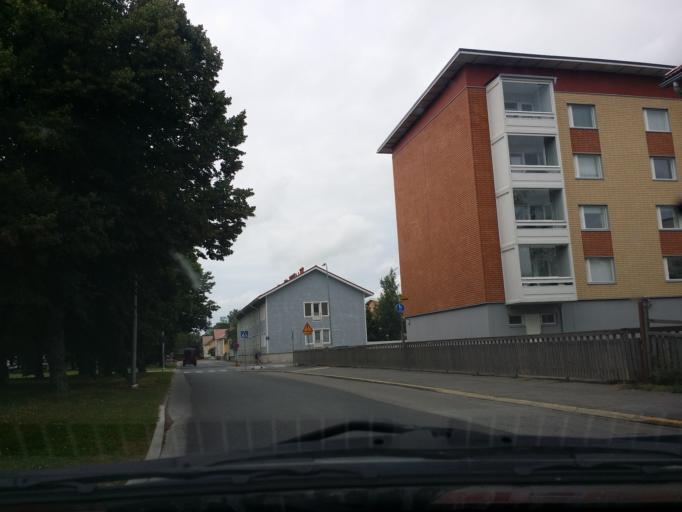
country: FI
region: Satakunta
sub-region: Pori
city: Pori
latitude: 61.4961
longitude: 21.8016
